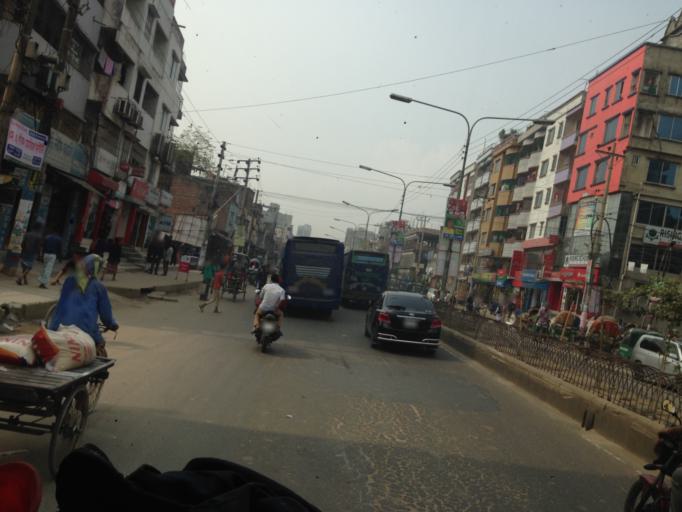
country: BD
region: Dhaka
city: Tungi
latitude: 23.8211
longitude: 90.3729
